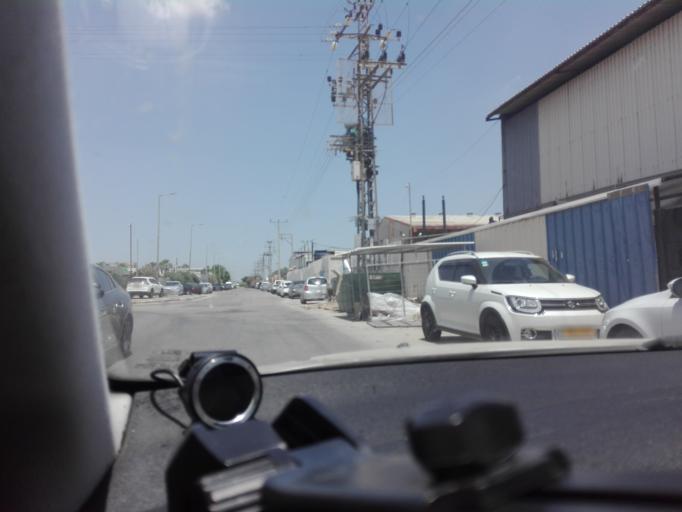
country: IL
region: Central District
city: Bene 'Ayish
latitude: 31.7368
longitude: 34.7531
